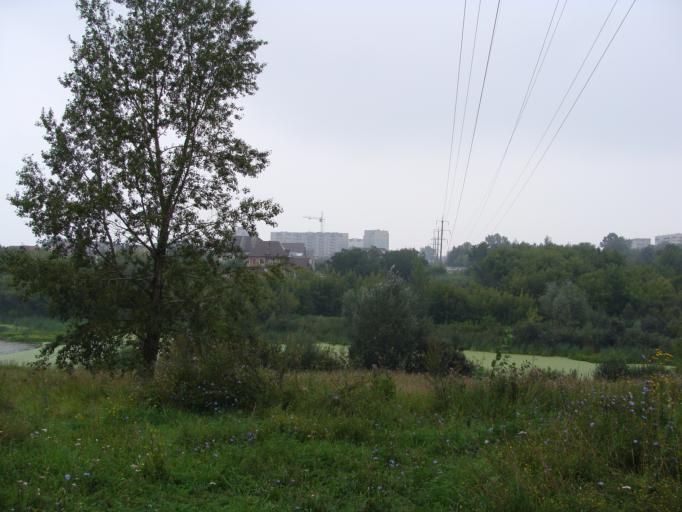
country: RU
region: Altai Krai
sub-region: Gorod Barnaulskiy
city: Barnaul
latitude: 53.3724
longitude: 83.7096
